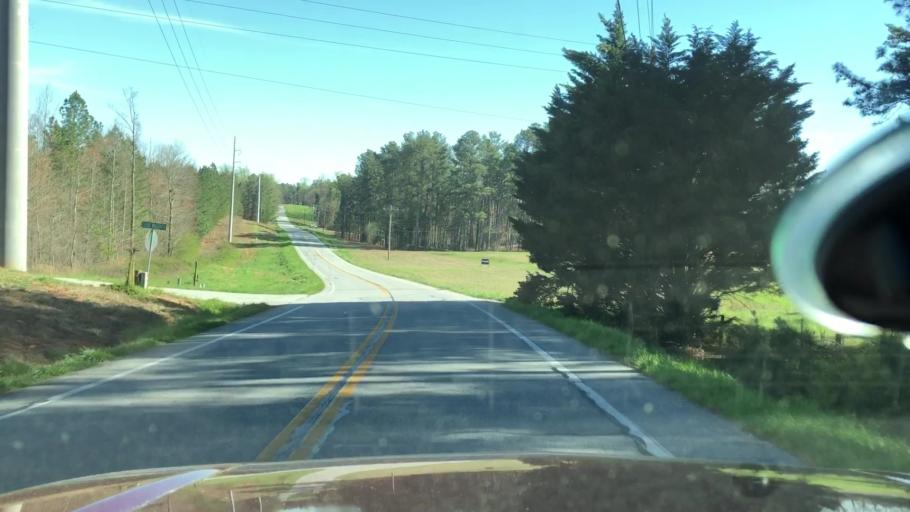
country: US
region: Georgia
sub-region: Dawson County
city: Dawsonville
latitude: 34.4555
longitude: -84.1723
